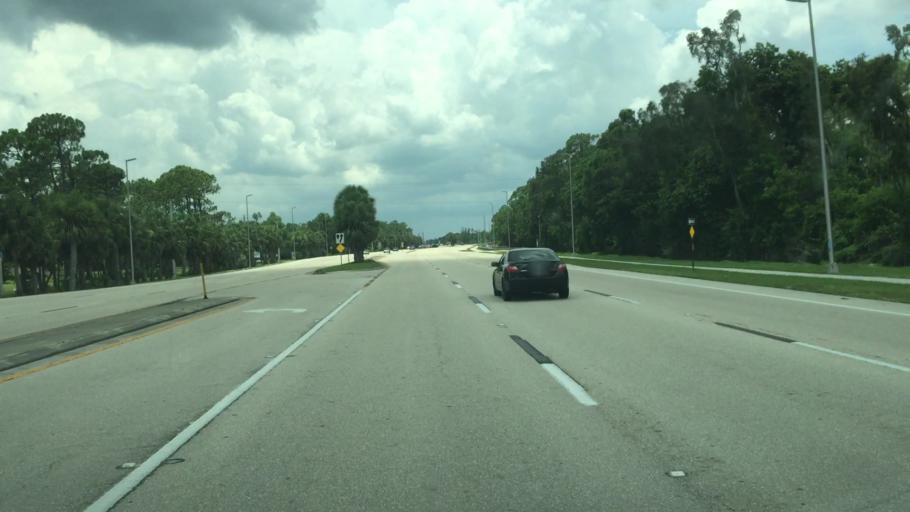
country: US
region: Florida
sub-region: Lee County
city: Villas
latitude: 26.5462
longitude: -81.8562
